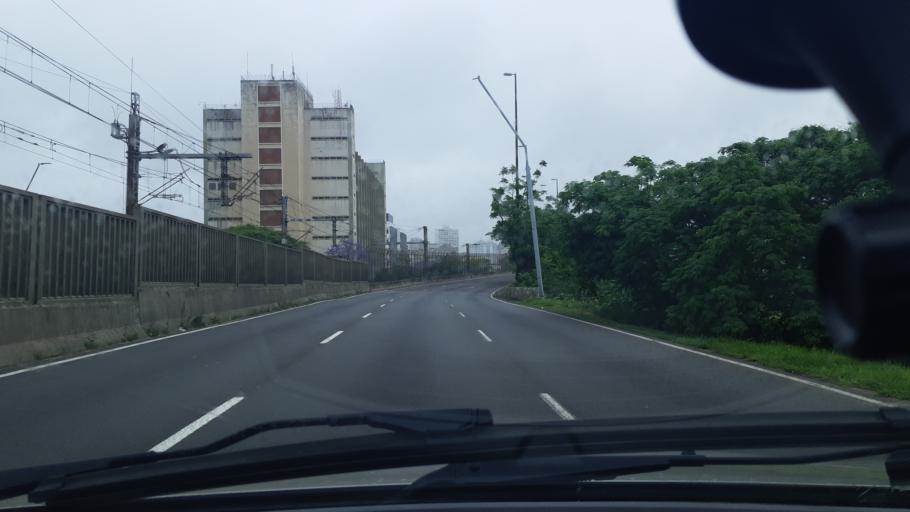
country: BR
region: Rio Grande do Sul
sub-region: Porto Alegre
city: Porto Alegre
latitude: -30.0195
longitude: -51.2164
